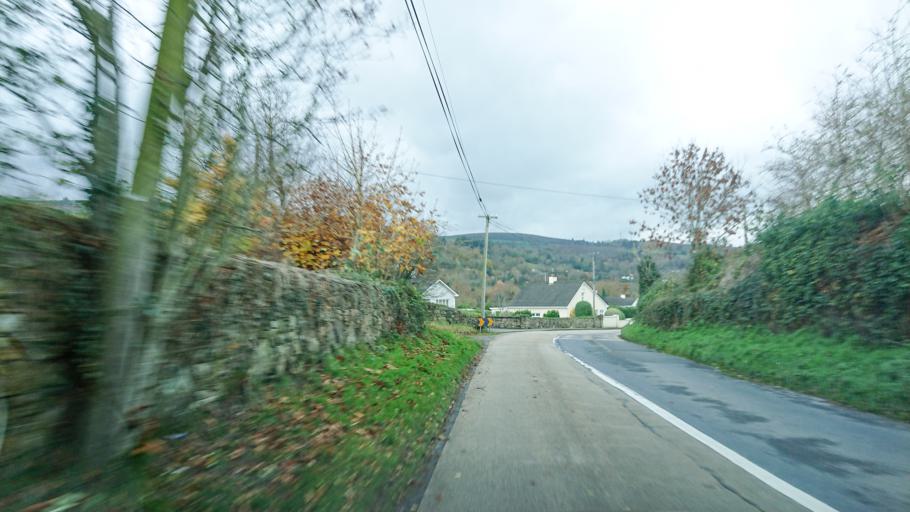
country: IE
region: Munster
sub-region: South Tipperary
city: Cluain Meala
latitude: 52.3535
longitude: -7.6724
